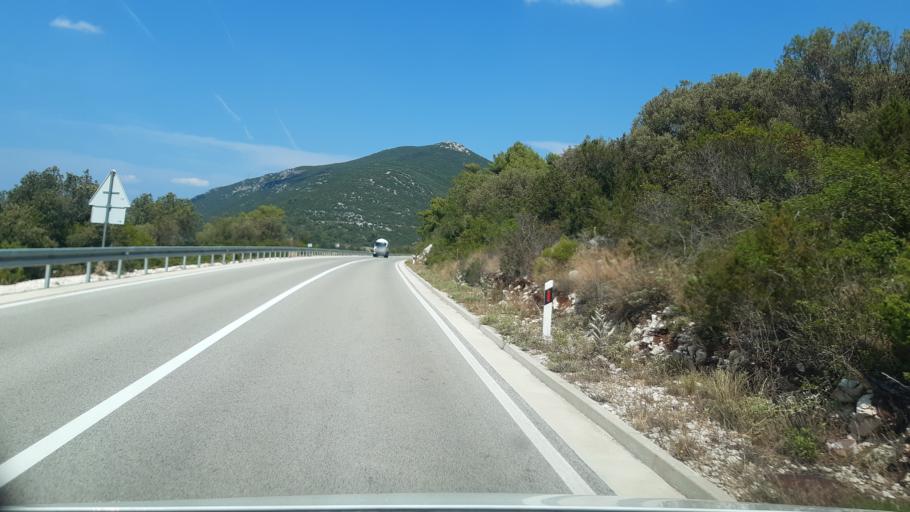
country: HR
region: Dubrovacko-Neretvanska
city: Ston
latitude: 42.8592
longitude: 17.7060
